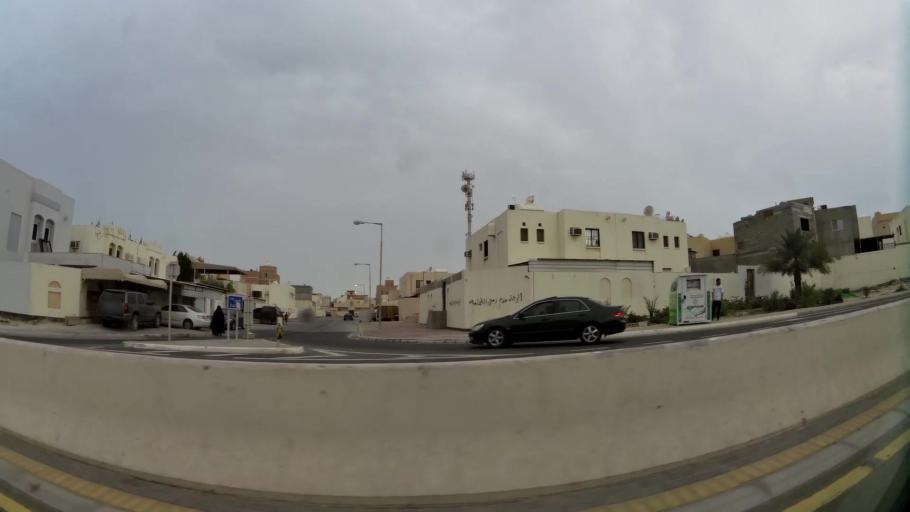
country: BH
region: Central Governorate
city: Dar Kulayb
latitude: 26.0834
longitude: 50.5050
